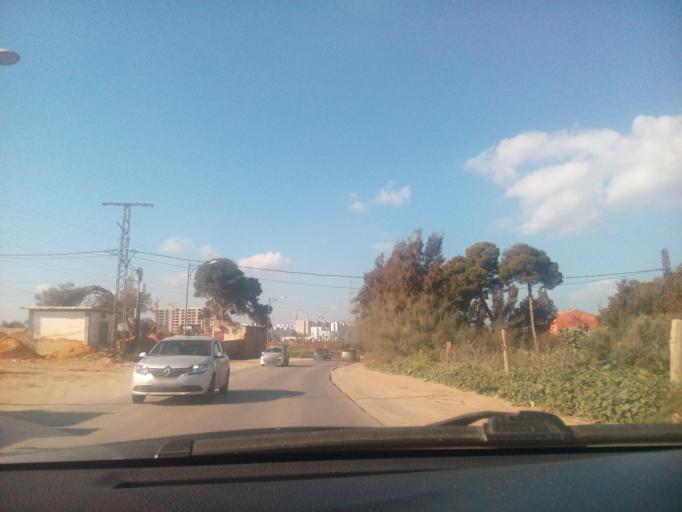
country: DZ
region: Oran
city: Es Senia
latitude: 35.6760
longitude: -0.5945
